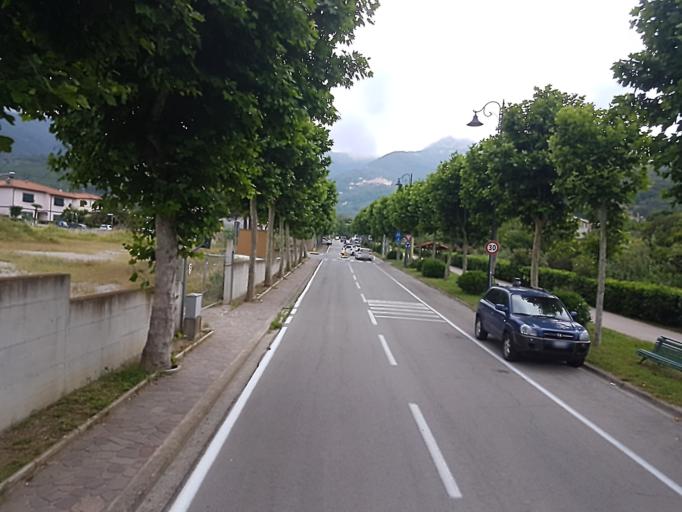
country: IT
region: Tuscany
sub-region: Provincia di Livorno
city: Marciana Marina
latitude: 42.8059
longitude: 10.1928
